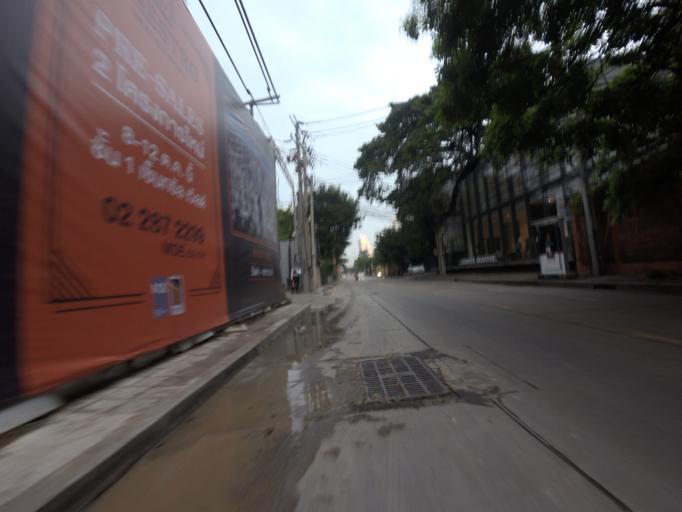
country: TH
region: Bangkok
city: Watthana
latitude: 13.7320
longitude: 100.5830
